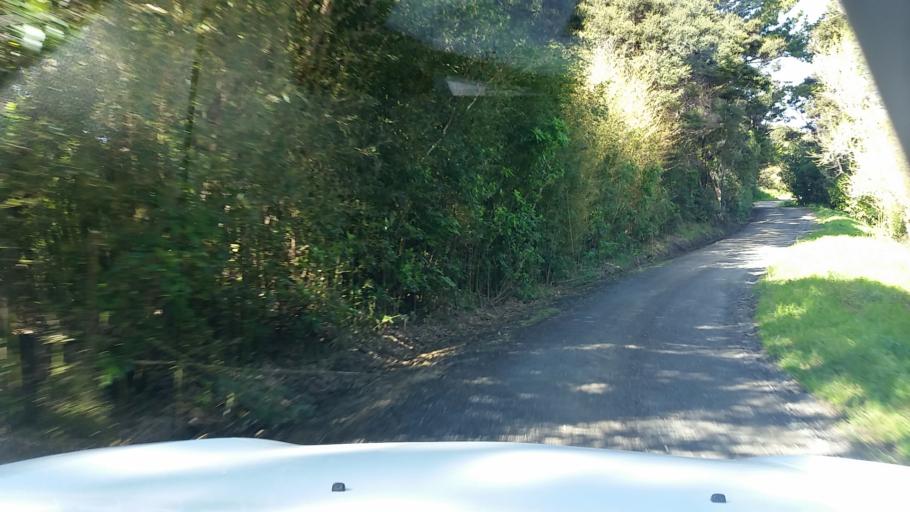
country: NZ
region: Auckland
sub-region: Auckland
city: Titirangi
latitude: -36.9817
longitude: 174.6129
